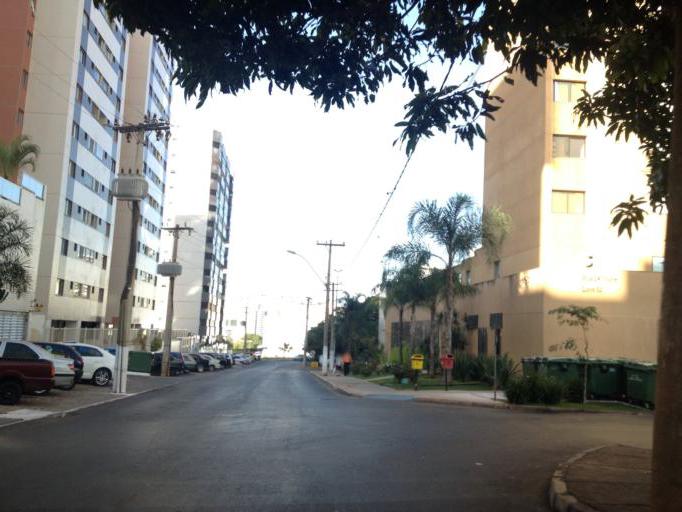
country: BR
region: Federal District
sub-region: Brasilia
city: Brasilia
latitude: -15.8371
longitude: -48.0288
